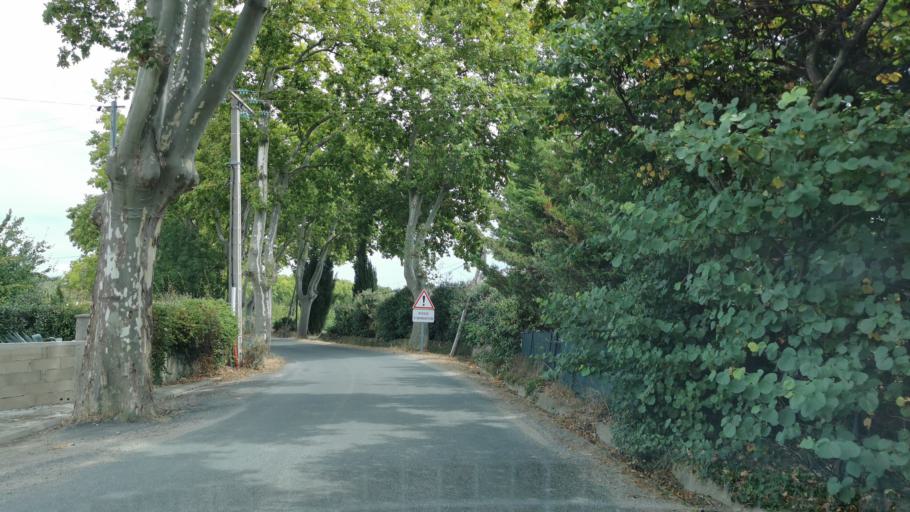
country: FR
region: Languedoc-Roussillon
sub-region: Departement de l'Aude
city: Bize-Minervois
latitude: 43.3036
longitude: 2.8294
